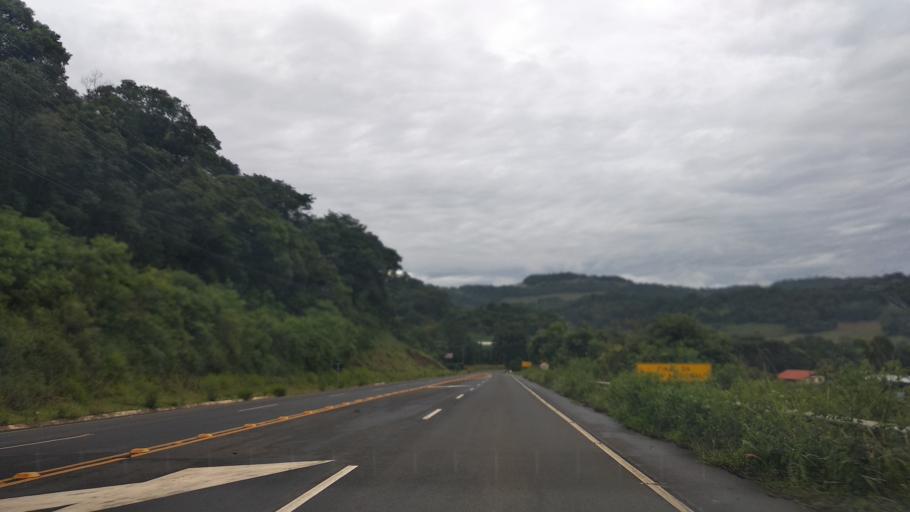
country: BR
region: Santa Catarina
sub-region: Videira
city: Videira
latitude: -27.0418
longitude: -51.1547
